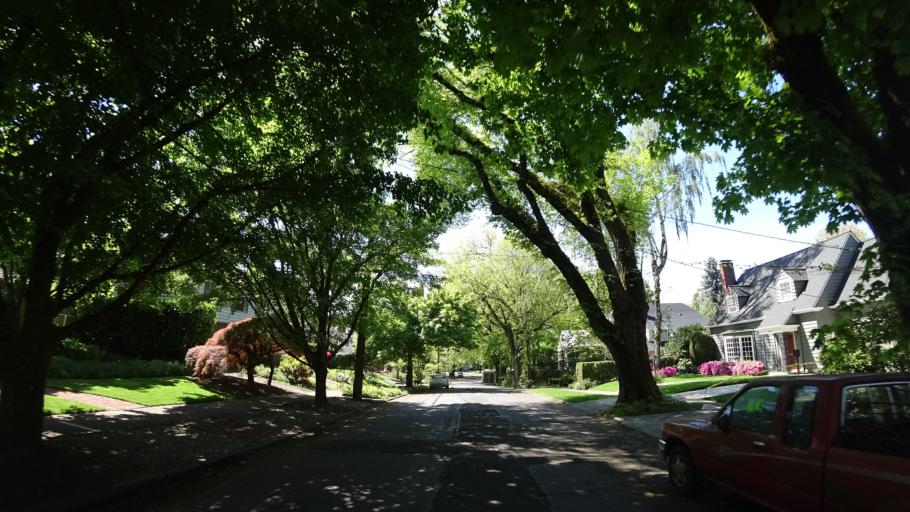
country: US
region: Oregon
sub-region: Clackamas County
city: Milwaukie
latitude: 45.4771
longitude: -122.6272
